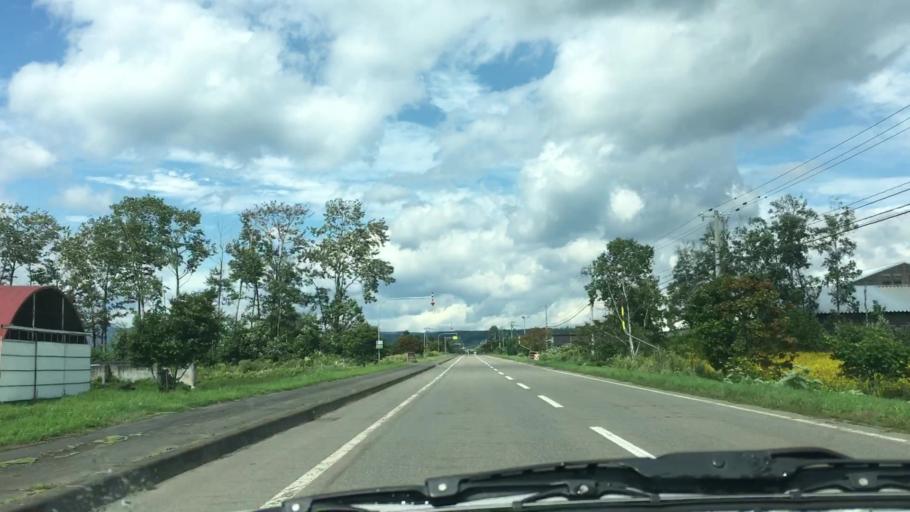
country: JP
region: Hokkaido
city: Otofuke
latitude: 43.2866
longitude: 143.3072
